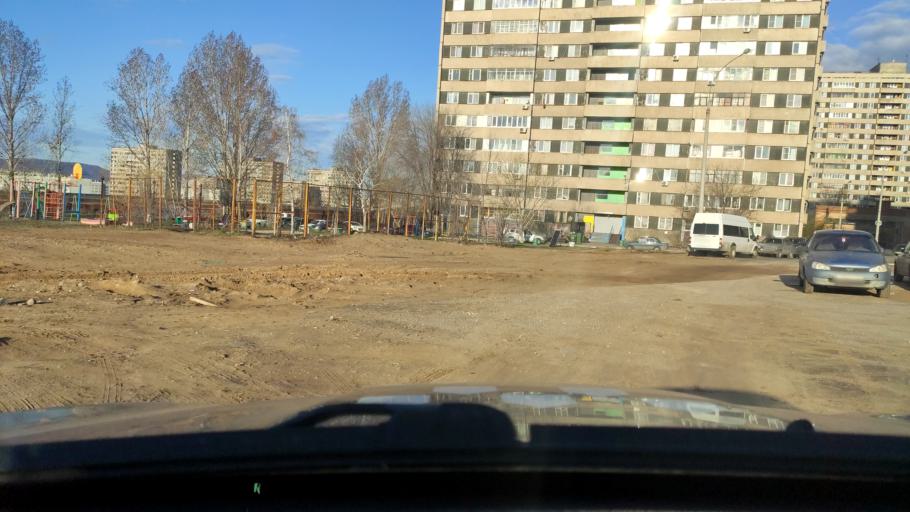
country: RU
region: Samara
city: Zhigulevsk
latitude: 53.4800
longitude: 49.5279
